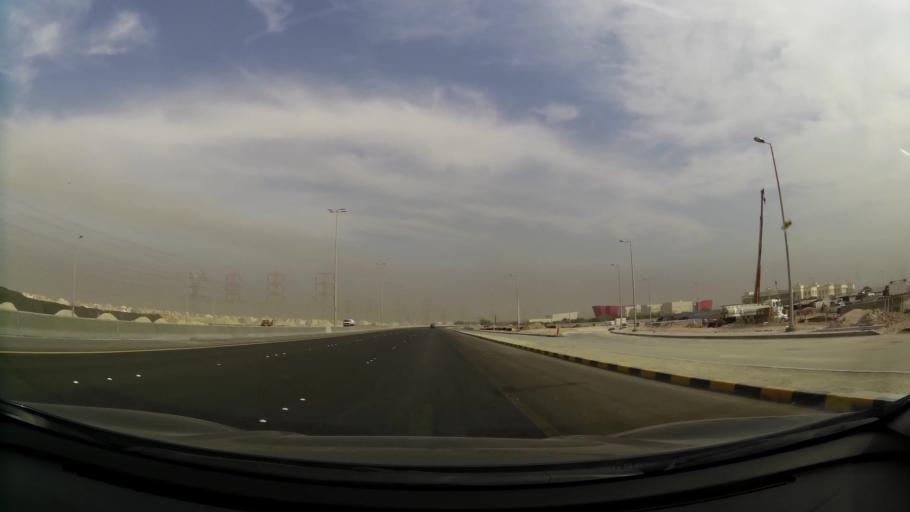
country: KW
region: Muhafazat al Jahra'
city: Al Jahra'
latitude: 29.3194
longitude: 47.7851
